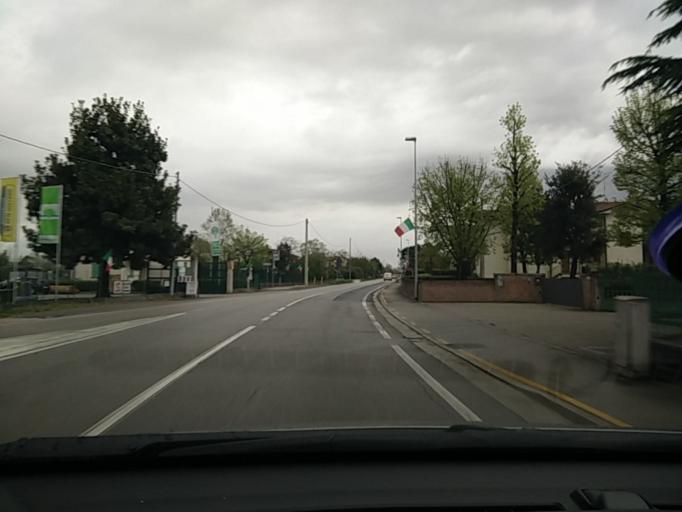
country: IT
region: Veneto
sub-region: Provincia di Treviso
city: Roncade
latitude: 45.6326
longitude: 12.3831
